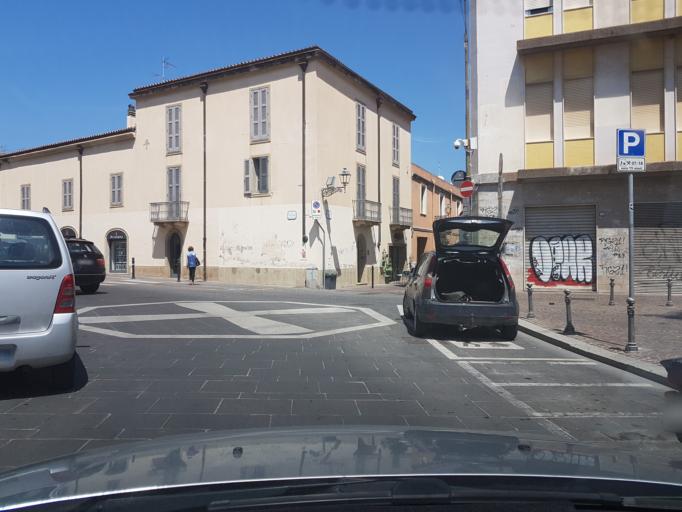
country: IT
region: Sardinia
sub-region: Provincia di Oristano
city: Oristano
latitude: 39.9037
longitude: 8.5904
